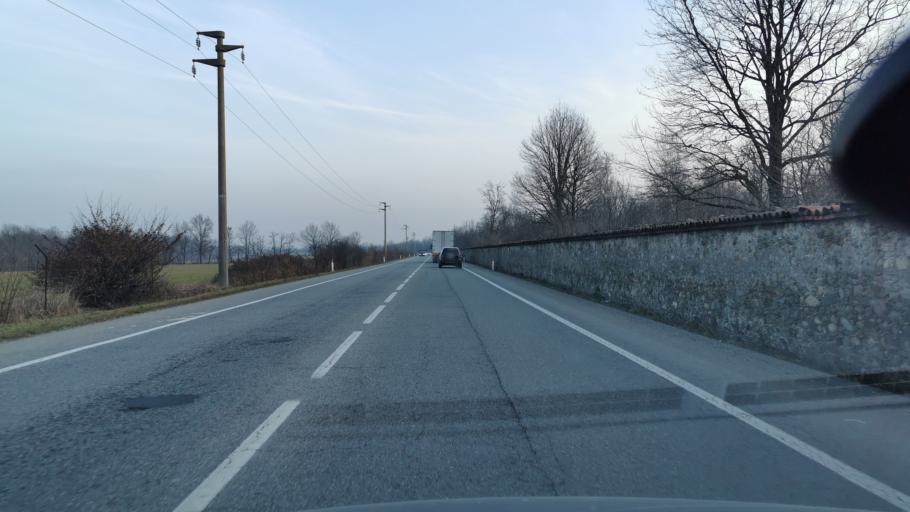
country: IT
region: Piedmont
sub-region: Provincia di Torino
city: Druento
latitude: 45.1665
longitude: 7.5955
